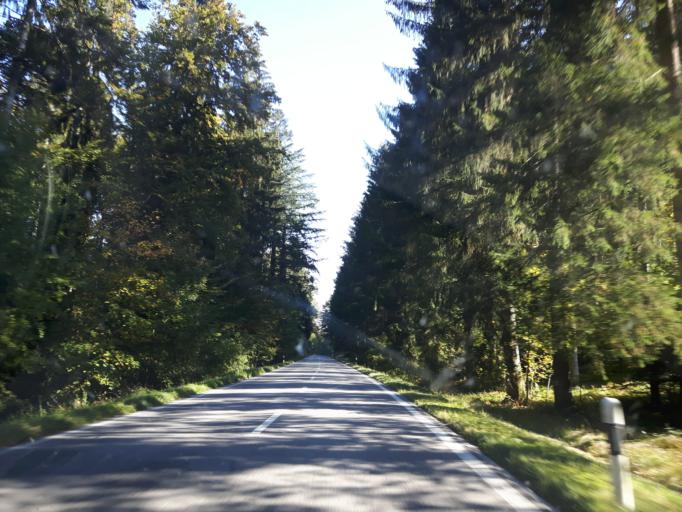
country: CH
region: Bern
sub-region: Oberaargau
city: Roggwil
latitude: 47.2479
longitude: 7.8427
